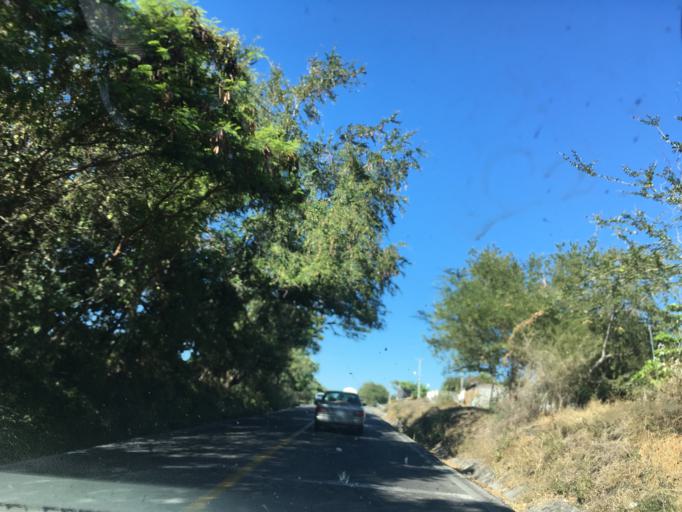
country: MX
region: Michoacan
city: Nueva Italia de Ruiz
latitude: 19.0866
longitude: -102.0588
